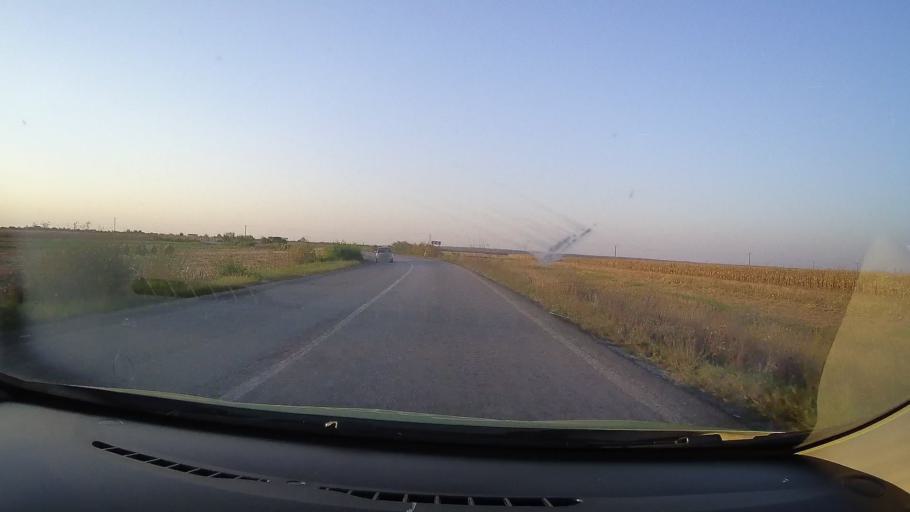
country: RO
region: Arad
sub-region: Comuna Ineu
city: Ineu
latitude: 46.4335
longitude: 21.8587
